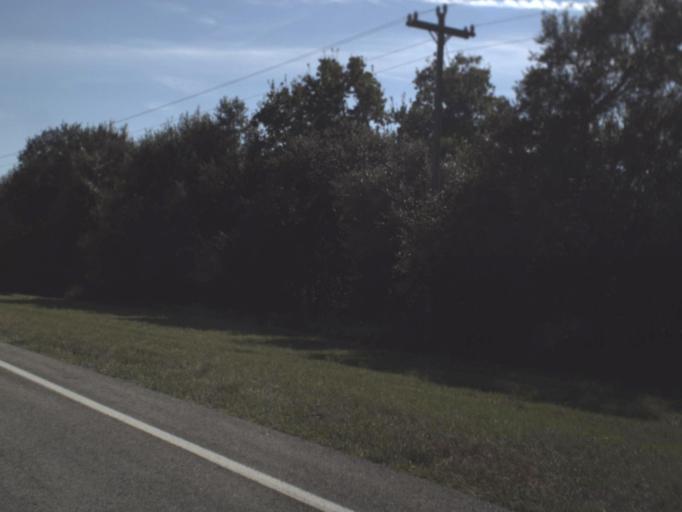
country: US
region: Florida
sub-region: Highlands County
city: Placid Lakes
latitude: 27.0283
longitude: -81.3418
